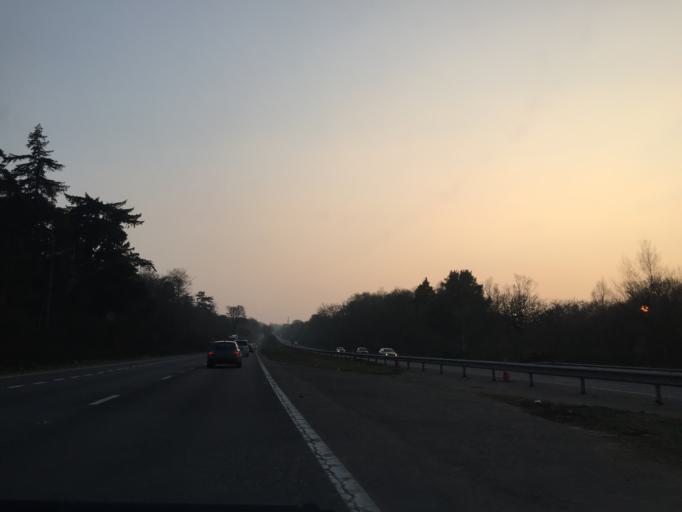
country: GB
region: England
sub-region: Hampshire
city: Cadnam
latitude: 50.9171
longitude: -1.5943
